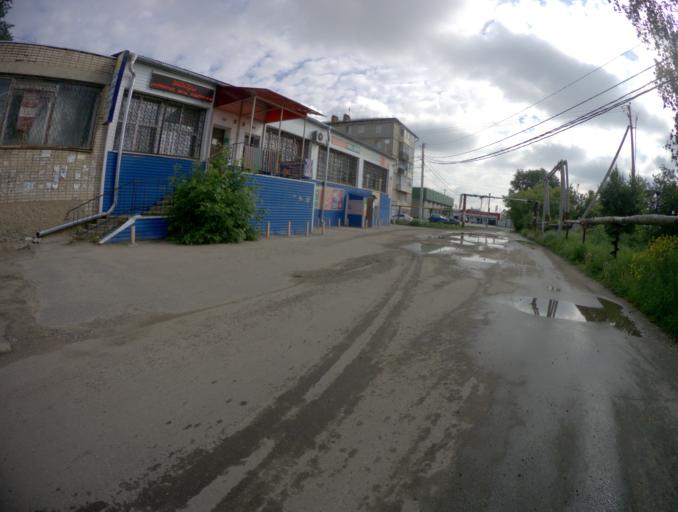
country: RU
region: Vladimir
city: Lakinsk
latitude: 56.0218
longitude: 39.9778
